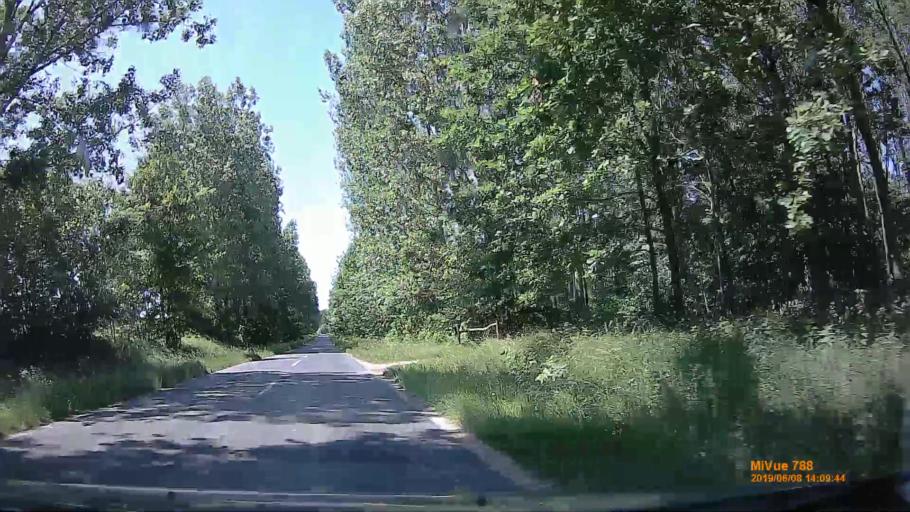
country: HU
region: Vas
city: Buk
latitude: 47.3695
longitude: 16.7345
